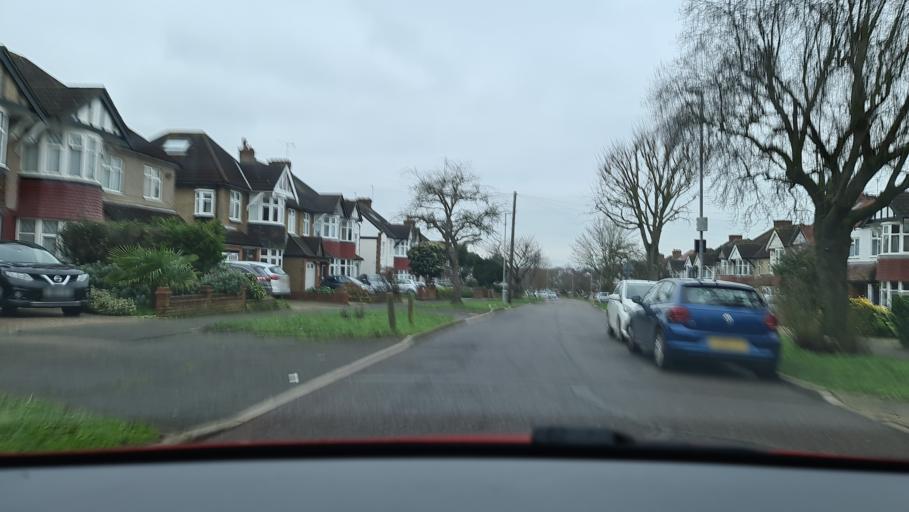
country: GB
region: England
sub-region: Greater London
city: New Malden
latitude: 51.3881
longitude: -0.2753
